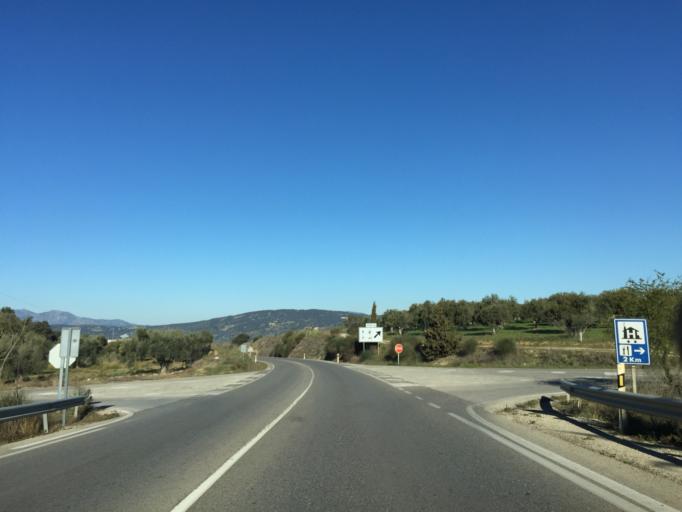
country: ES
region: Andalusia
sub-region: Provincia de Malaga
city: Ronda
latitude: 36.7583
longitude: -5.1569
